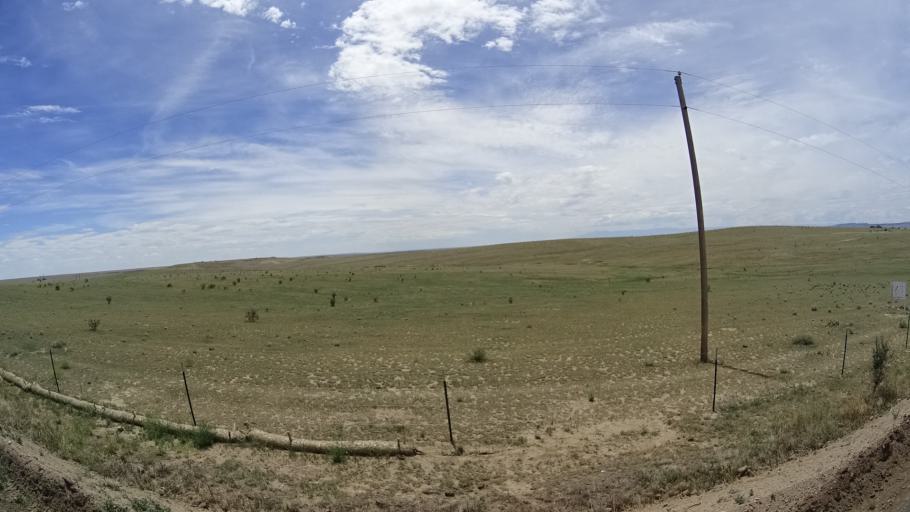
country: US
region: Colorado
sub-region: El Paso County
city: Fountain
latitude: 38.6940
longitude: -104.6445
